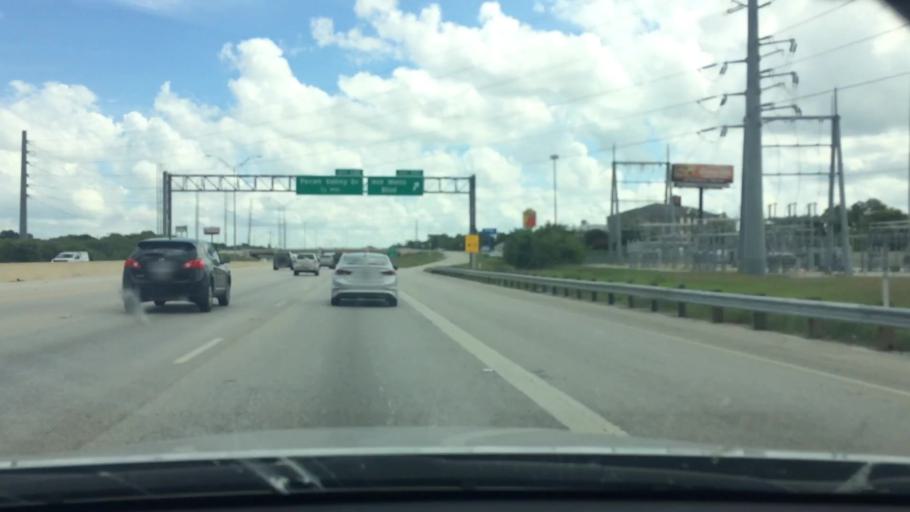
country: US
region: Texas
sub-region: Bexar County
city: San Antonio
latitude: 29.3713
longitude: -98.4551
